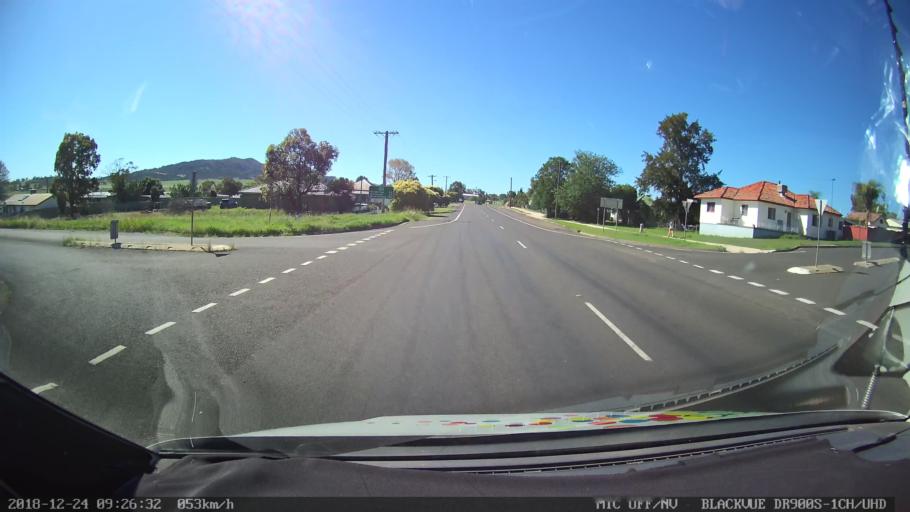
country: AU
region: New South Wales
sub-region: Liverpool Plains
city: Quirindi
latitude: -31.5206
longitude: 150.6773
